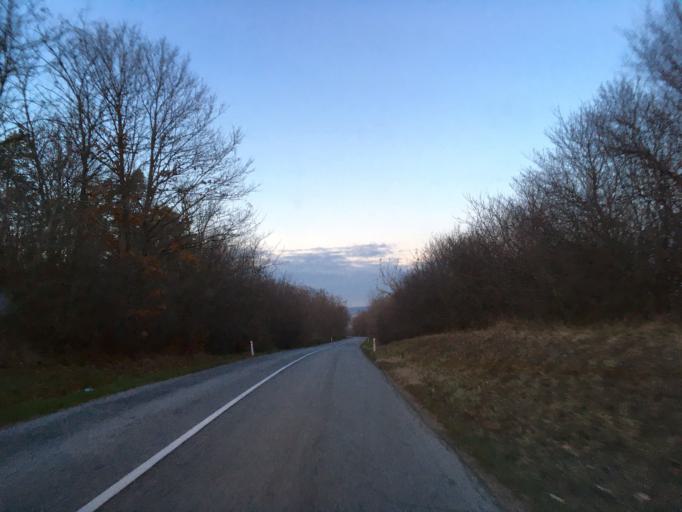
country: SK
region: Nitriansky
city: Svodin
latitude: 47.8640
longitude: 18.4596
